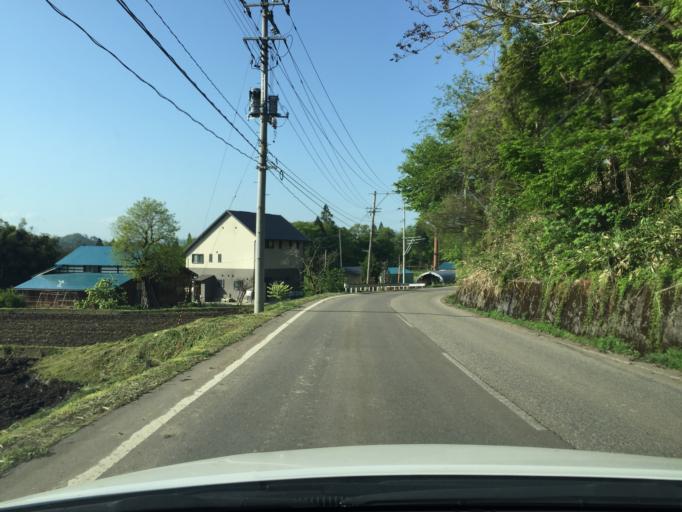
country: JP
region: Fukushima
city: Kitakata
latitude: 37.6618
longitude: 139.7760
